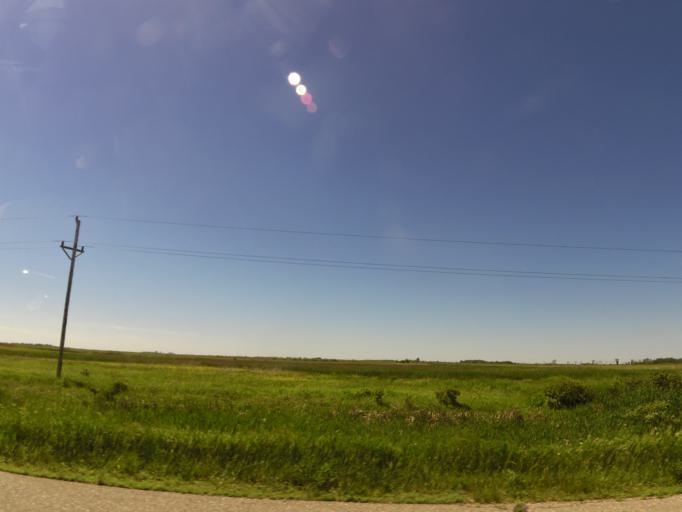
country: US
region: Minnesota
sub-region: Red Lake County
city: Red Lake Falls
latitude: 47.7604
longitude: -96.3702
